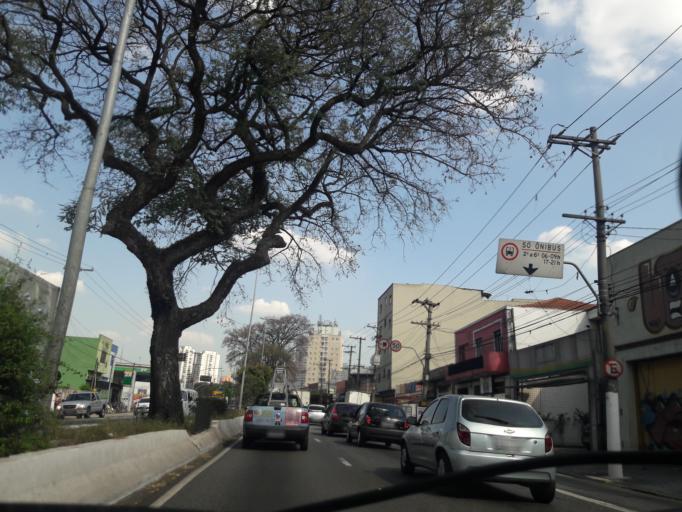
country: BR
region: Sao Paulo
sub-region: Sao Caetano Do Sul
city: Sao Caetano do Sul
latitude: -23.6160
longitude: -46.6015
